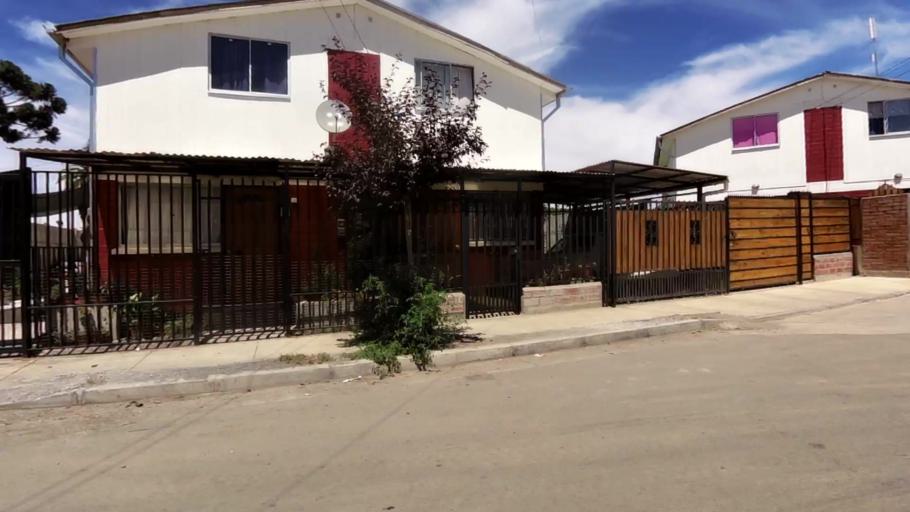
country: CL
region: O'Higgins
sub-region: Provincia de Cachapoal
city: Graneros
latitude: -34.0617
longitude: -70.7226
